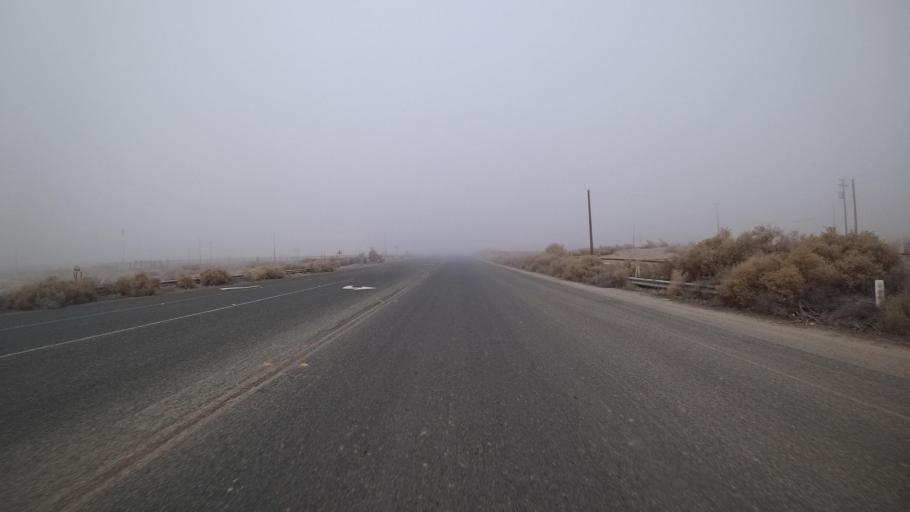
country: US
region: California
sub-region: Kern County
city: Buttonwillow
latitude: 35.2792
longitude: -119.4670
